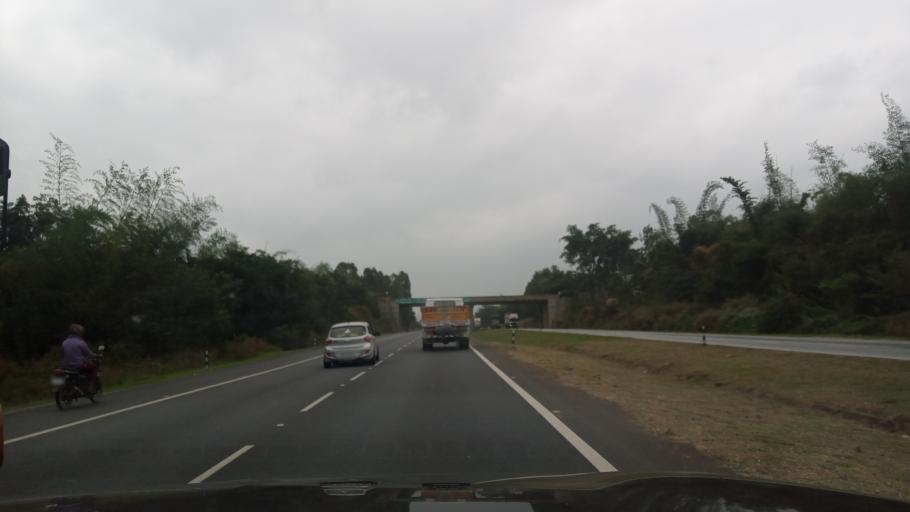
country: IN
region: Karnataka
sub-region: Bangalore Rural
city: Nelamangala
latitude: 13.0276
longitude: 77.4755
